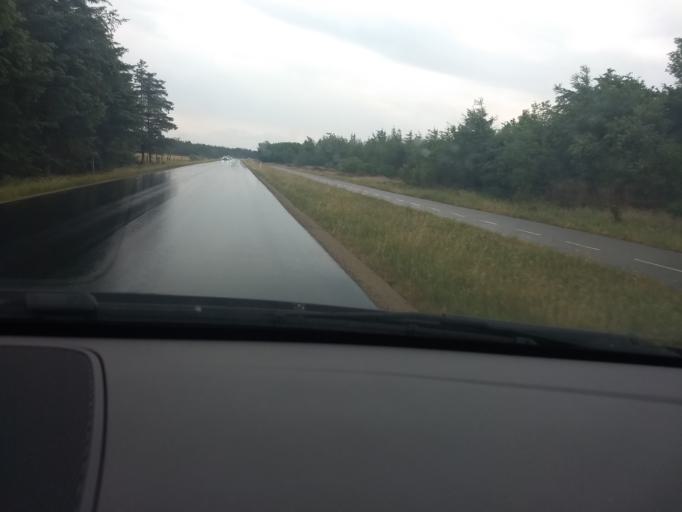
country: DK
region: South Denmark
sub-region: Fano Kommune
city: Nordby
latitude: 55.4080
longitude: 8.4145
